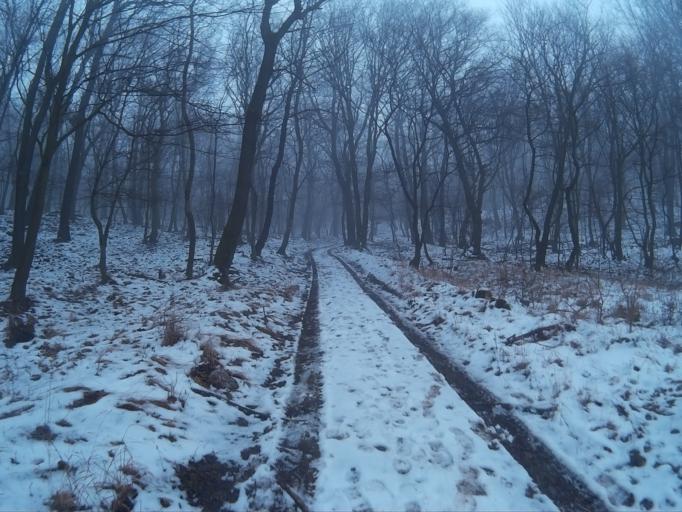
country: HU
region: Komarom-Esztergom
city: Tardos
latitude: 47.6635
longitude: 18.4755
